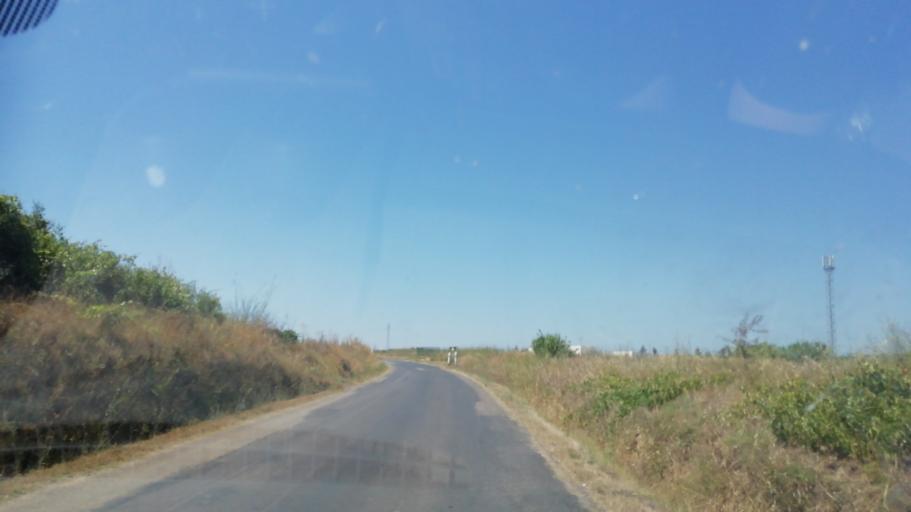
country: FR
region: Languedoc-Roussillon
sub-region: Departement de l'Herault
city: Maraussan
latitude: 43.3655
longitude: 3.1483
